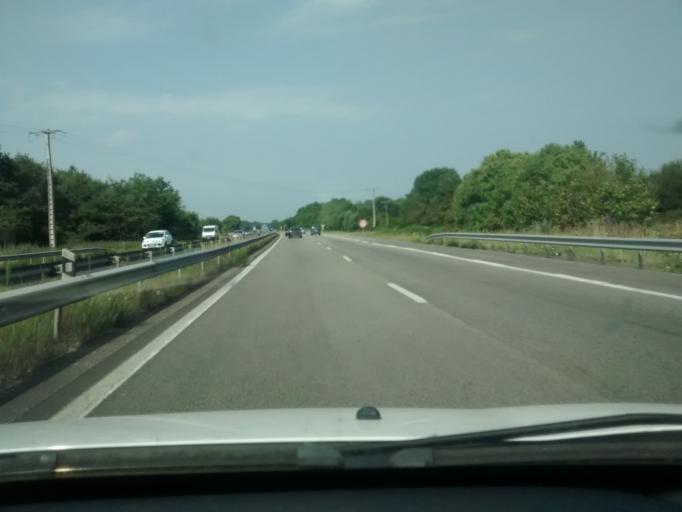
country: FR
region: Pays de la Loire
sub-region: Departement de la Loire-Atlantique
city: Prinquiau
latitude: 47.3575
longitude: -2.0062
